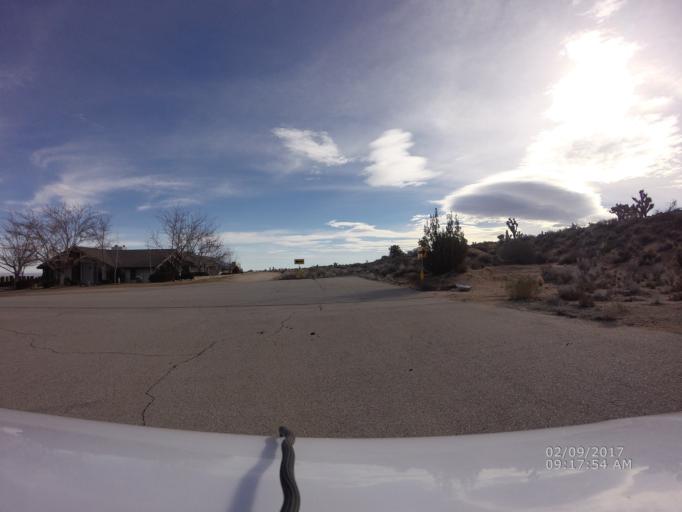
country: US
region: California
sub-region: Los Angeles County
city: Lake Los Angeles
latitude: 34.4689
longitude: -117.8433
